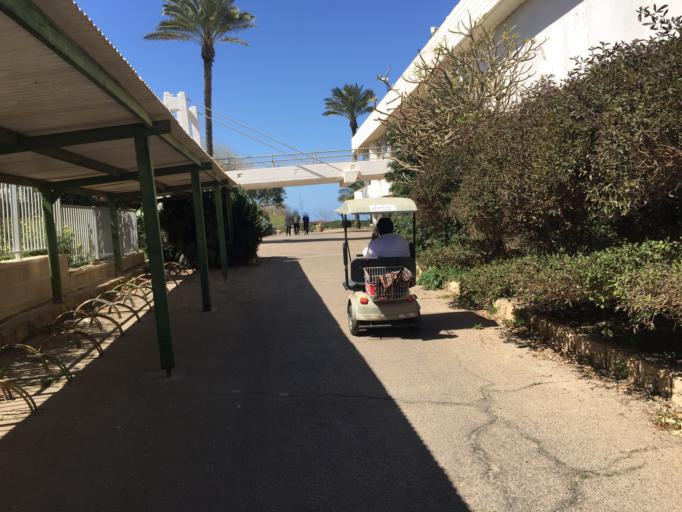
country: IL
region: Haifa
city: Qesarya
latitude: 32.4932
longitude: 34.8913
